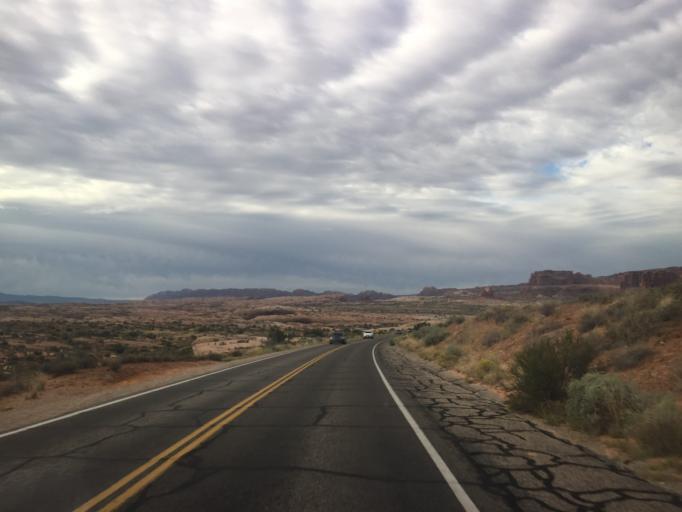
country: US
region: Utah
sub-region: Grand County
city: Moab
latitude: 38.6605
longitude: -109.5881
